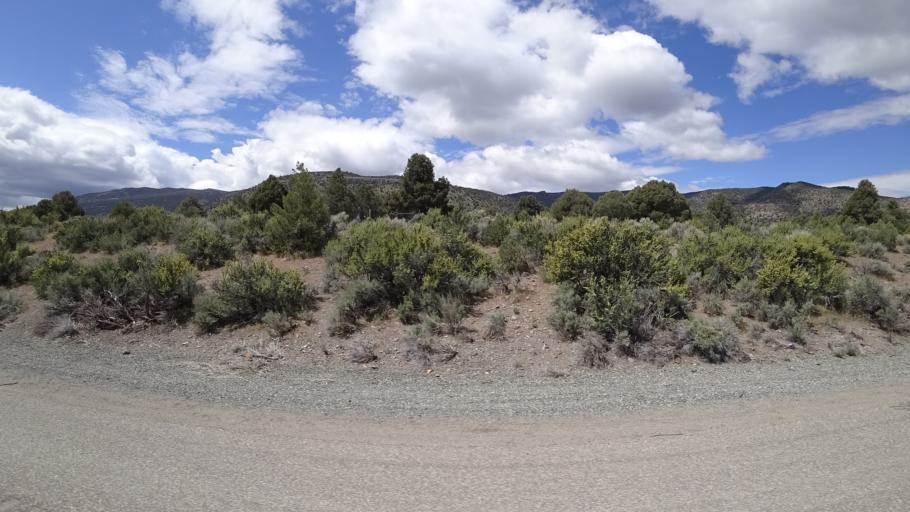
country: US
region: Nevada
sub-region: Lyon County
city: Smith Valley
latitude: 38.7437
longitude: -119.5645
